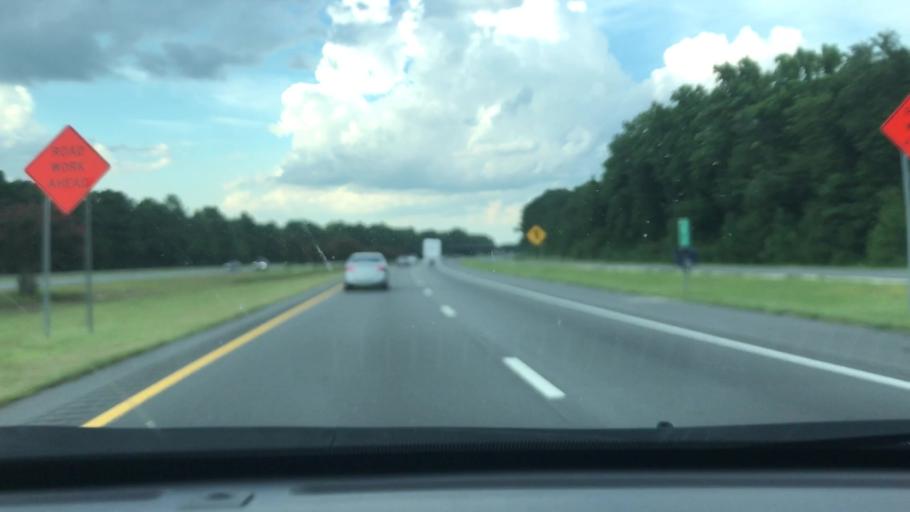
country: US
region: North Carolina
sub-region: Cumberland County
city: Vander
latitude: 35.0482
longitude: -78.8016
